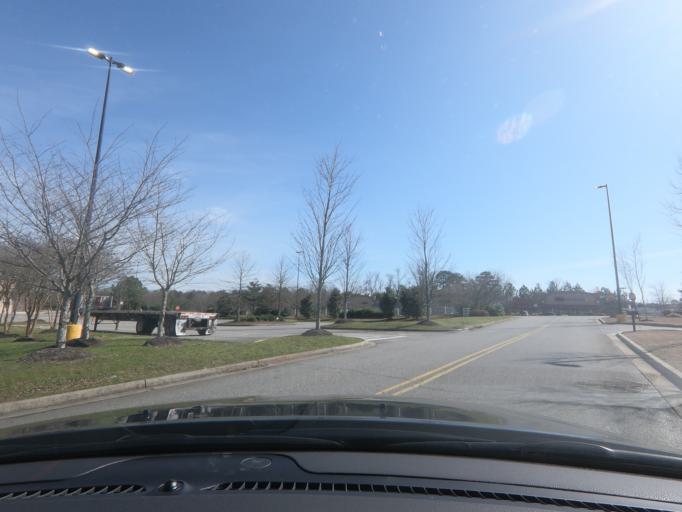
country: US
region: Georgia
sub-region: Fulton County
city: Milton
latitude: 34.1492
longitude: -84.2510
